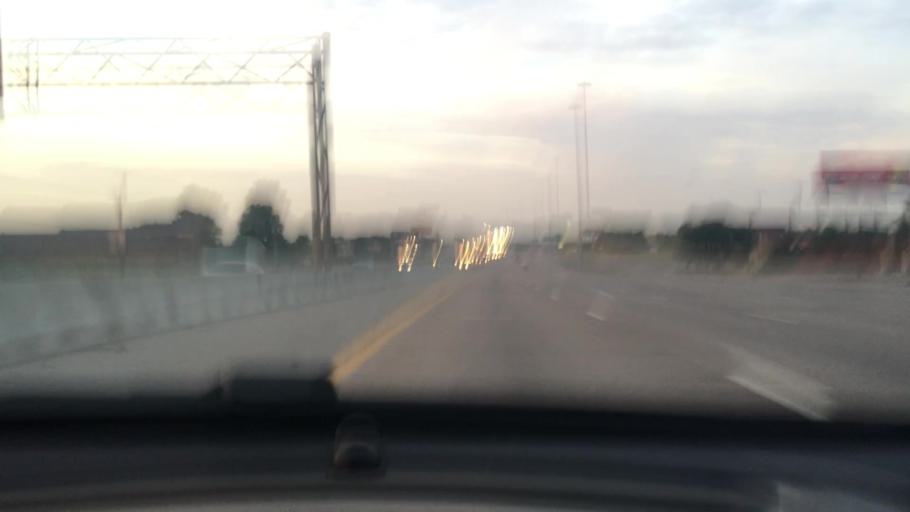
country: US
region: Texas
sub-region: Dallas County
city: Duncanville
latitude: 32.6710
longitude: -96.8226
